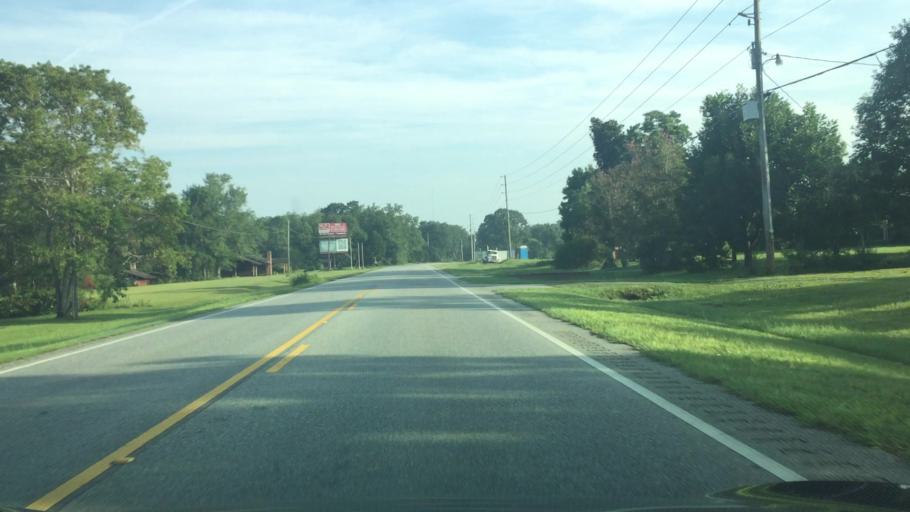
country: US
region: Alabama
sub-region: Covington County
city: Andalusia
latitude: 31.2672
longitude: -86.4731
